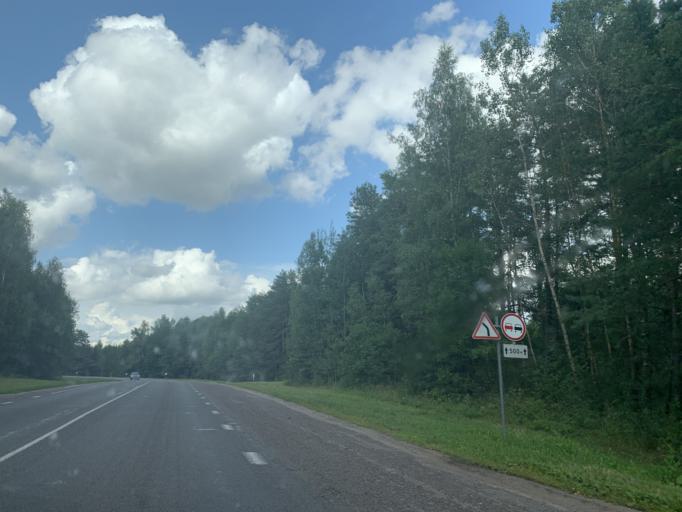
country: BY
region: Minsk
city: Enyerhyetykaw
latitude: 53.5681
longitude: 27.0631
